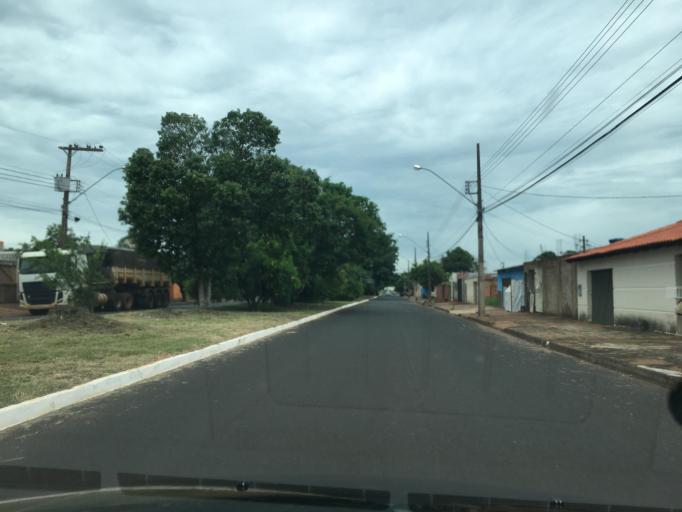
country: BR
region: Minas Gerais
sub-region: Uberlandia
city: Uberlandia
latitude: -18.8809
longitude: -48.2283
